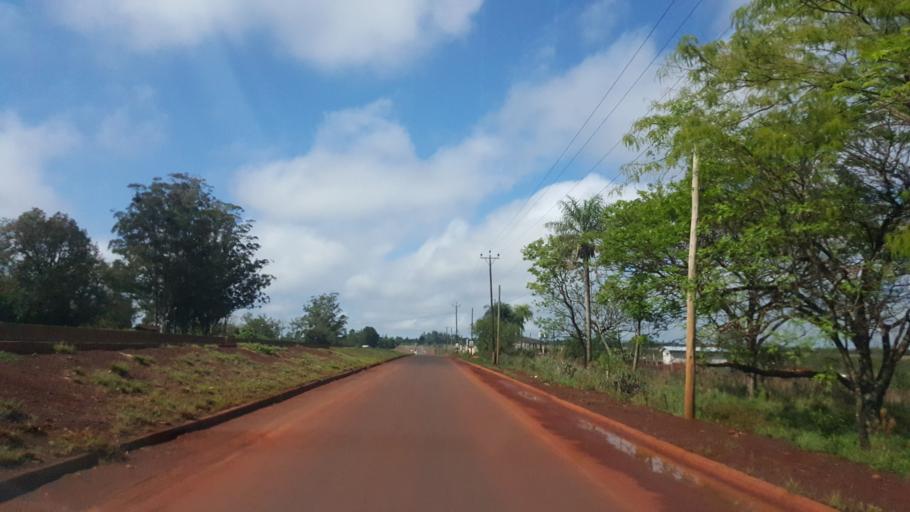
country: AR
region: Misiones
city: Garupa
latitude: -27.4820
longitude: -55.8639
